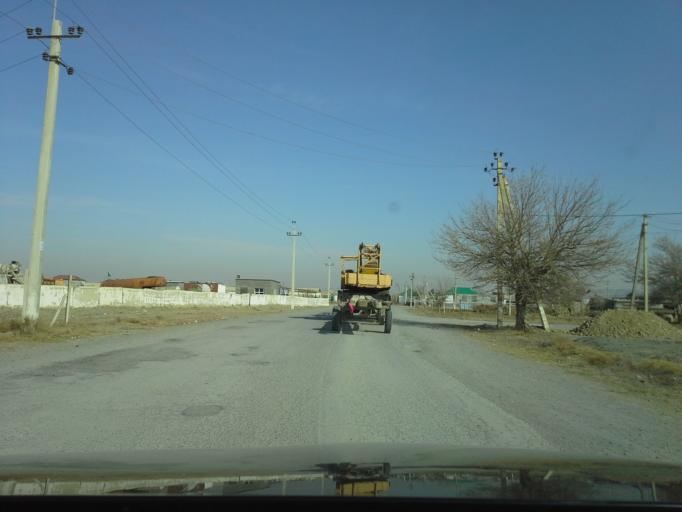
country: TM
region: Ahal
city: Abadan
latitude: 38.1198
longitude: 57.9943
